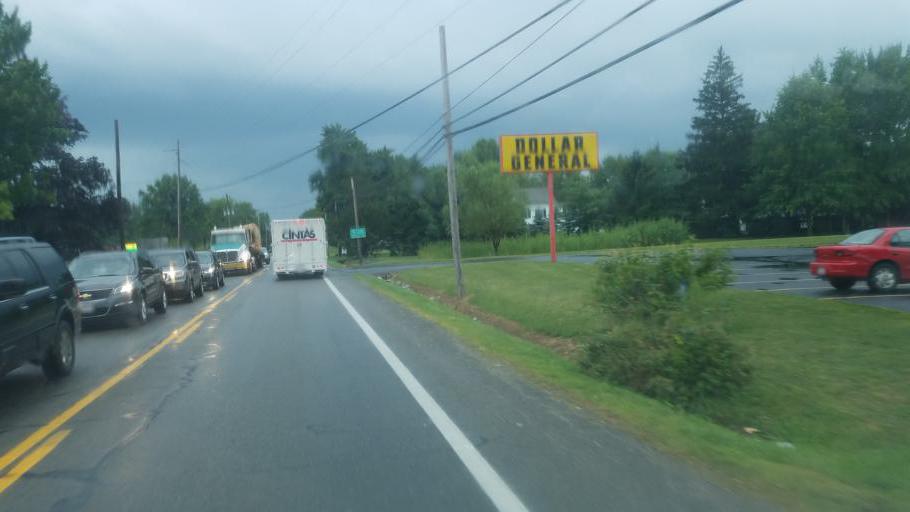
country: US
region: Ohio
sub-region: Trumbull County
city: Champion Heights
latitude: 41.3077
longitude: -80.8496
